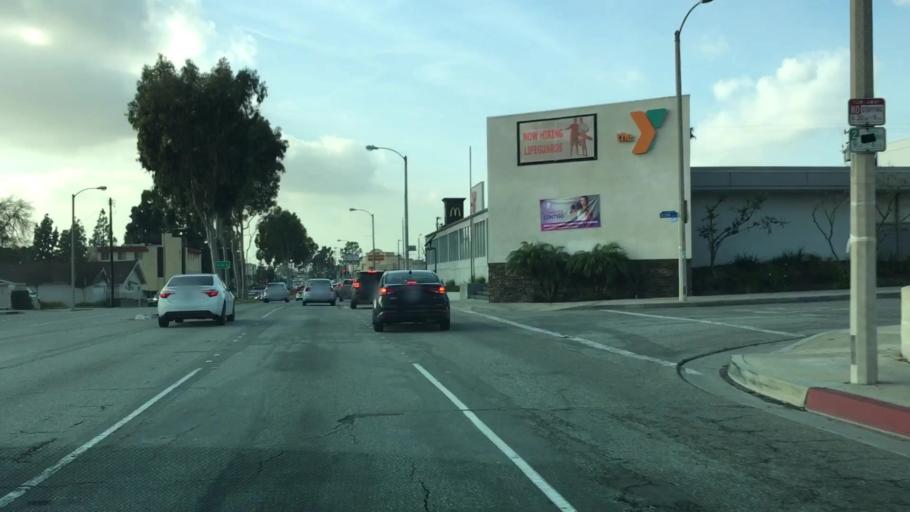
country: US
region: California
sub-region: Los Angeles County
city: Montebello
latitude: 34.0202
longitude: -118.1201
